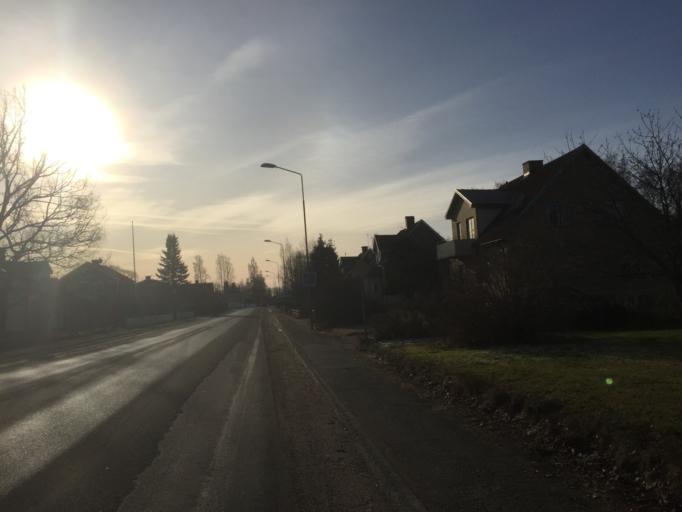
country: SE
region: Joenkoeping
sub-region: Aneby Kommun
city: Aneby
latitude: 57.8410
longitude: 14.8041
